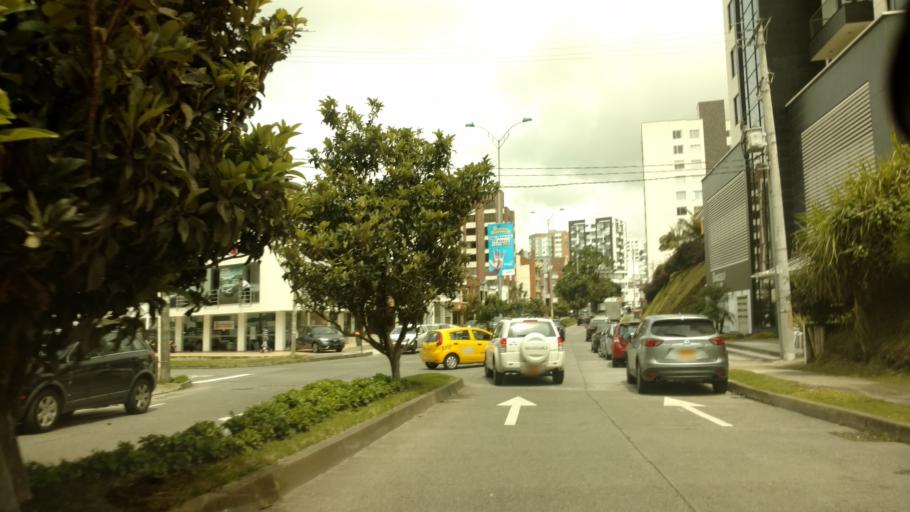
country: CO
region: Caldas
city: Villamaria
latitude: 5.0504
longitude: -75.4877
